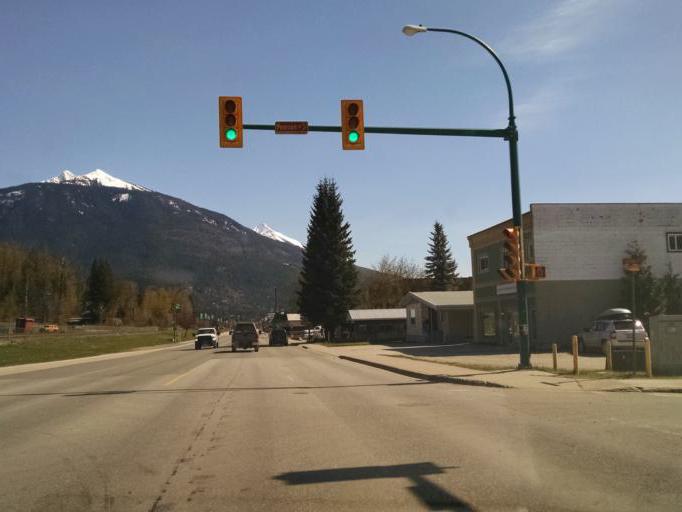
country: CA
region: British Columbia
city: Revelstoke
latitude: 51.0038
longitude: -118.2016
